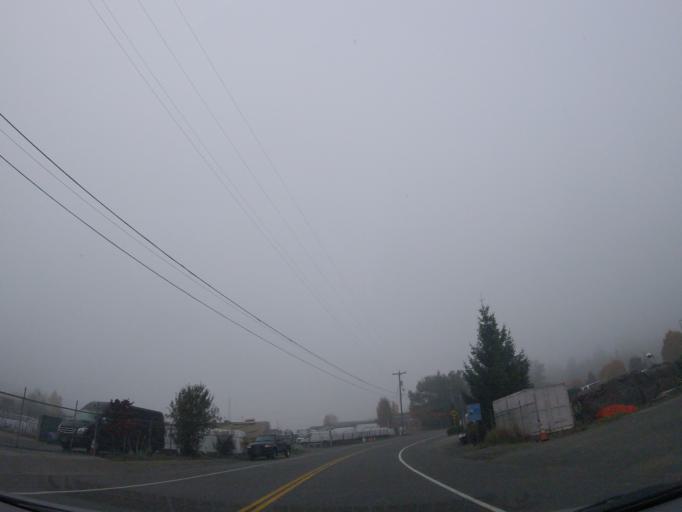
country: US
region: Washington
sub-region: King County
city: Kenmore
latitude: 47.7576
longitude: -122.2506
